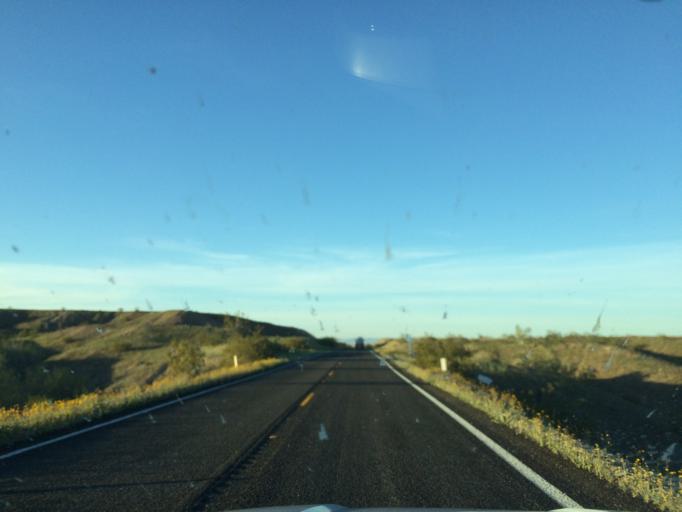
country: US
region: California
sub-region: Riverside County
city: Mesa Verde
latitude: 33.3462
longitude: -114.7232
